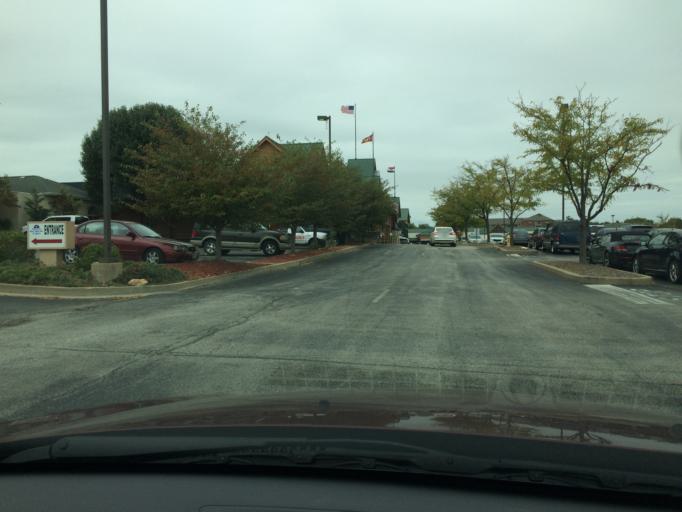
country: US
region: Missouri
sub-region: Saint Charles County
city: Saint Charles
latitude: 38.7710
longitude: -90.4959
